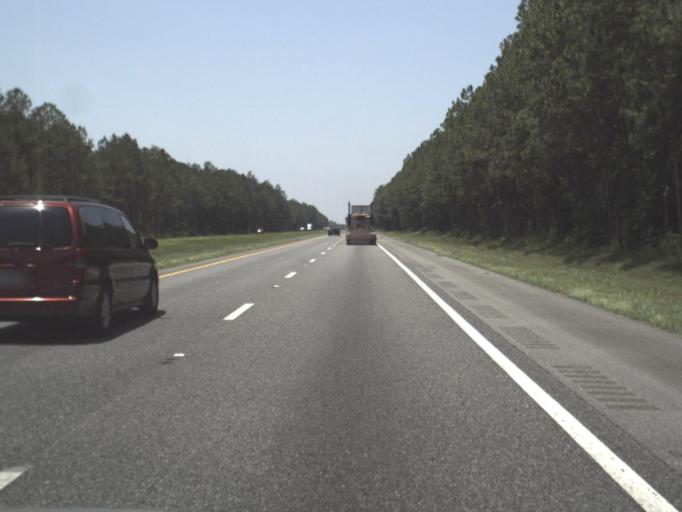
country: US
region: Florida
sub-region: Union County
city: Lake Butler
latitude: 30.2544
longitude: -82.3747
